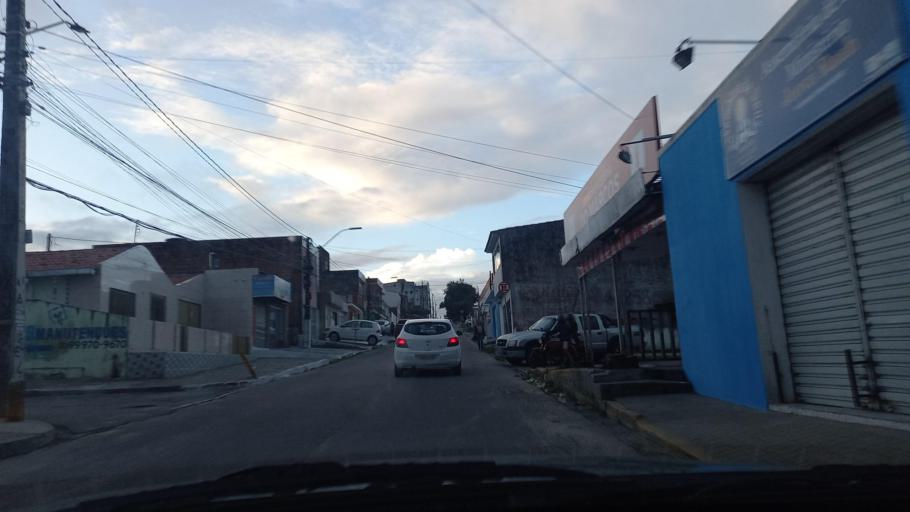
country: BR
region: Pernambuco
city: Garanhuns
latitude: -8.8843
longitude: -36.4664
